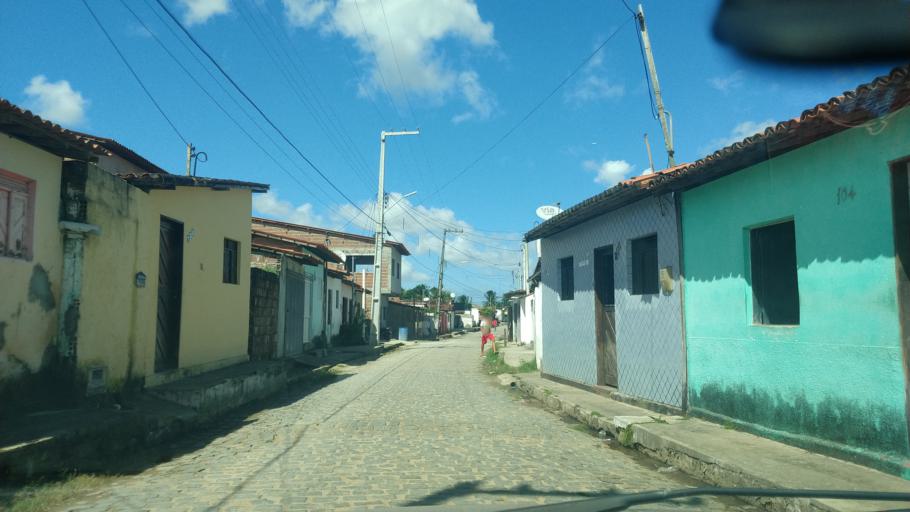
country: BR
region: Rio Grande do Norte
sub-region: Sao Goncalo Do Amarante
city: Sao Goncalo do Amarante
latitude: -5.8206
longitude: -35.3153
